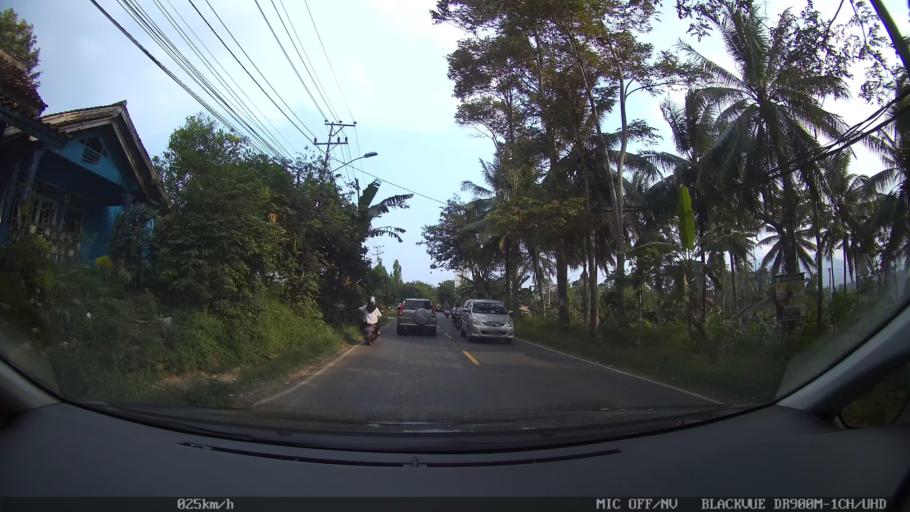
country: ID
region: Lampung
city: Natar
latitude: -5.3657
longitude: 105.1880
